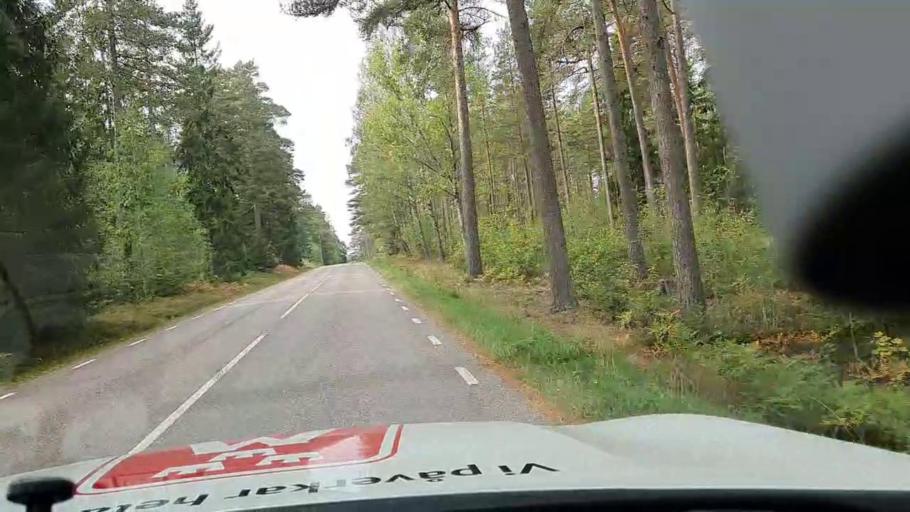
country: SE
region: Soedermanland
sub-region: Nykopings Kommun
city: Stigtomta
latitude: 58.8081
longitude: 16.8004
